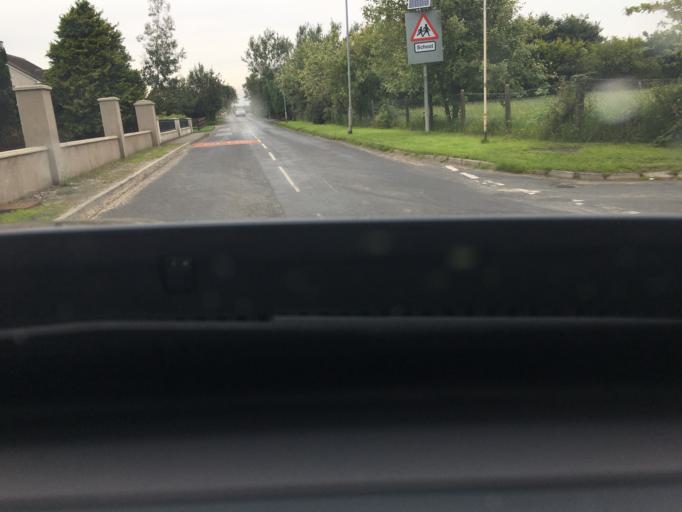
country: GB
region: Northern Ireland
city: Coalisland
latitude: 54.5381
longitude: -6.6207
